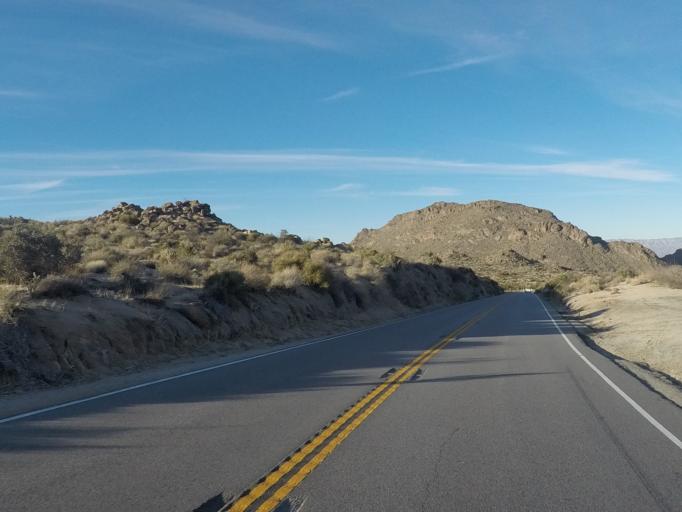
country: US
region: California
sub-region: Riverside County
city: Palm Desert
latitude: 33.6153
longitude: -116.4150
